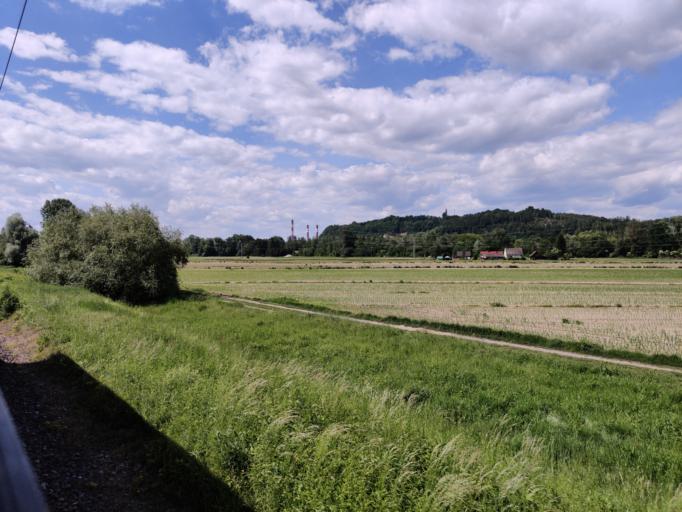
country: AT
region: Styria
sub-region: Politischer Bezirk Leibnitz
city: Wildon
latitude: 46.8903
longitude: 15.5052
